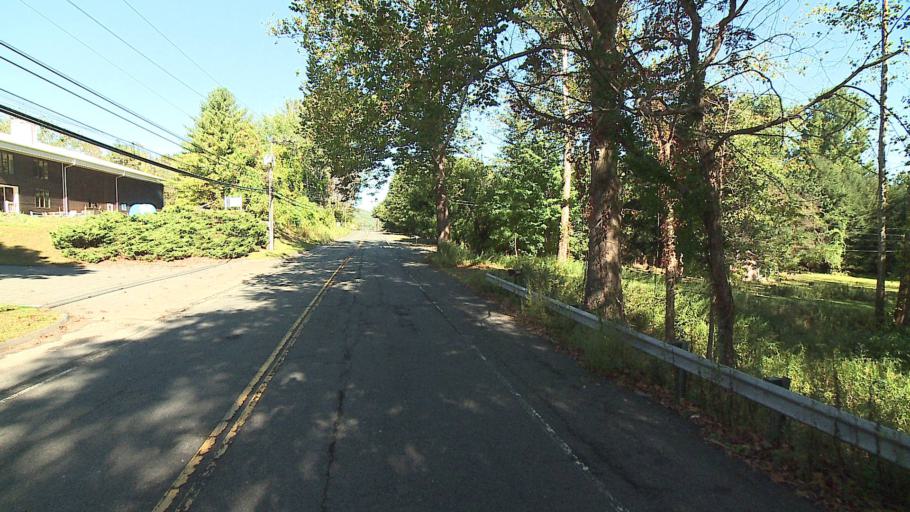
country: US
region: Connecticut
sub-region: Litchfield County
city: New Milford
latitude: 41.4863
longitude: -73.4119
